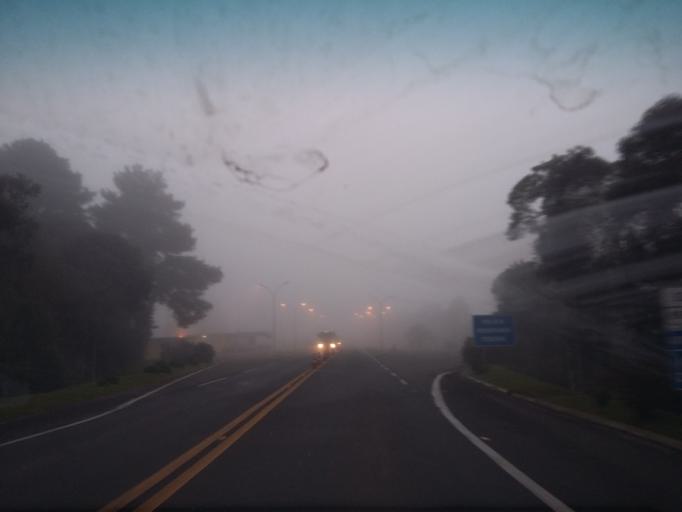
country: BR
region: Santa Catarina
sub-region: Correia Pinto
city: Correia Pinto
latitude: -27.4290
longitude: -50.4097
